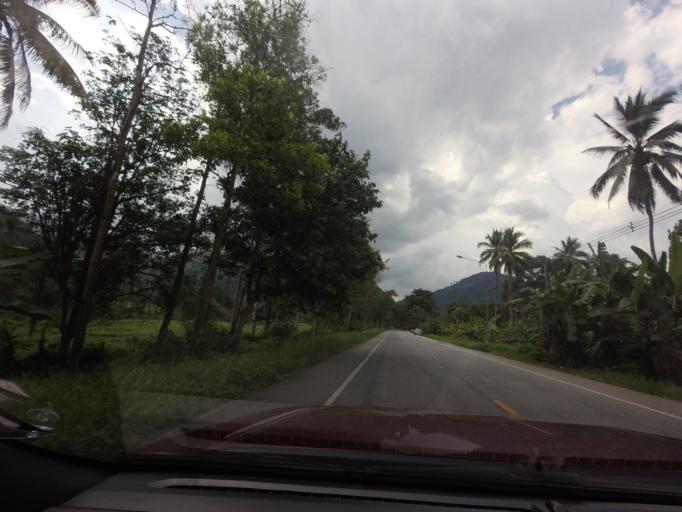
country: TH
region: Yala
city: Than To
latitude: 6.1905
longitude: 101.1726
